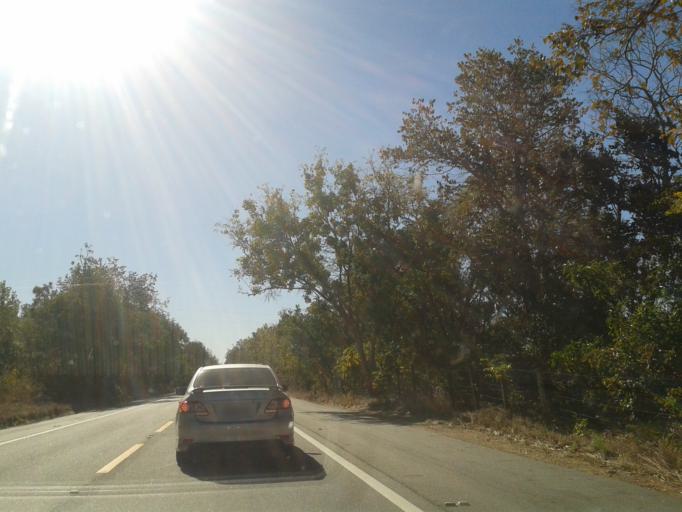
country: BR
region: Goias
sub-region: Itapuranga
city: Itapuranga
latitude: -15.5002
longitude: -50.3064
